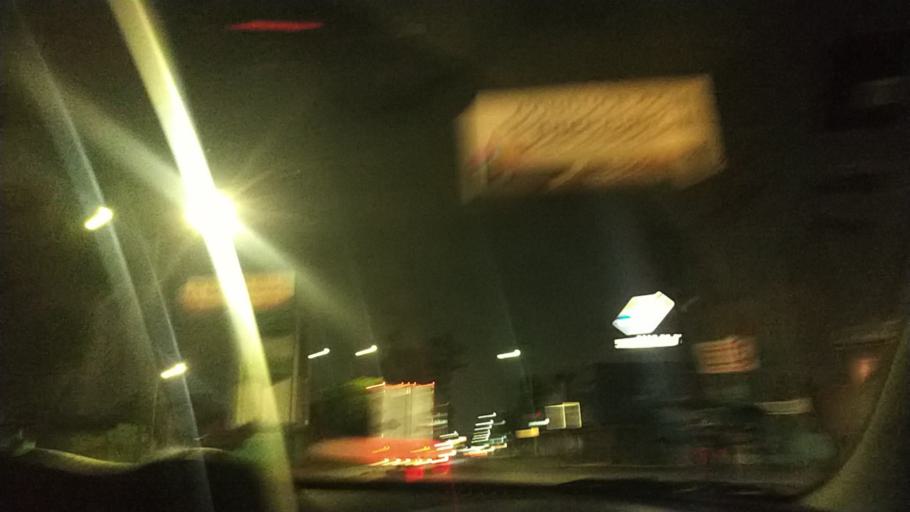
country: MX
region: Mexico
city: Ecatepec
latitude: 19.6227
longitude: -99.0736
